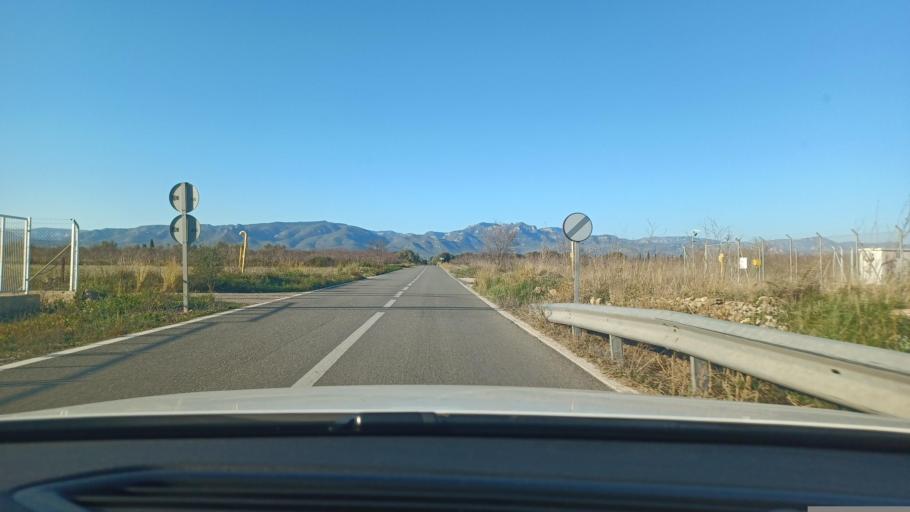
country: ES
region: Catalonia
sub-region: Provincia de Tarragona
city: Ulldecona
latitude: 40.6298
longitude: 0.3634
